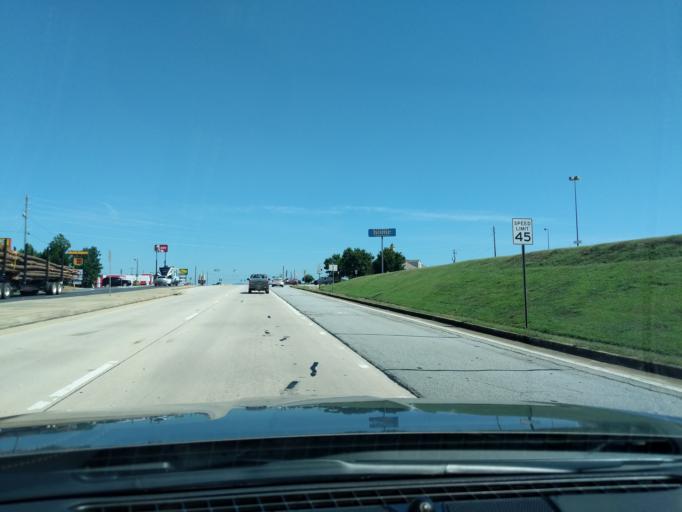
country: US
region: Georgia
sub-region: Habersham County
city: Baldwin
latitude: 34.5080
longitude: -83.5452
